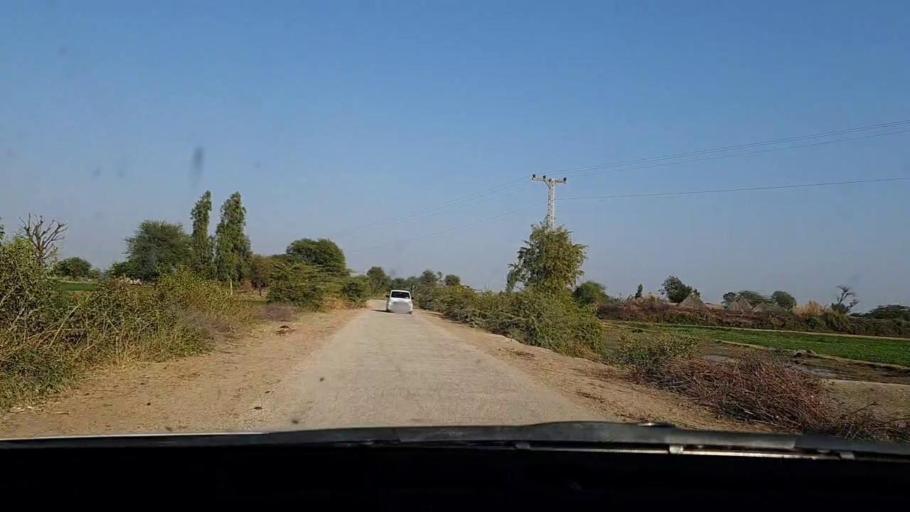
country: PK
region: Sindh
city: Tando Mittha Khan
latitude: 25.8350
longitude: 69.3305
